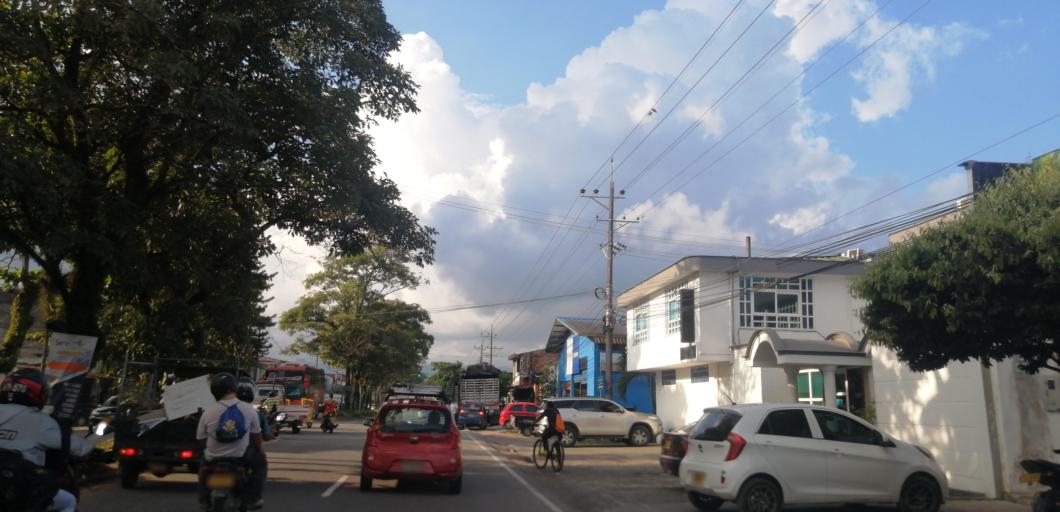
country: CO
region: Meta
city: Acacias
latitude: 3.9831
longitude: -73.7665
